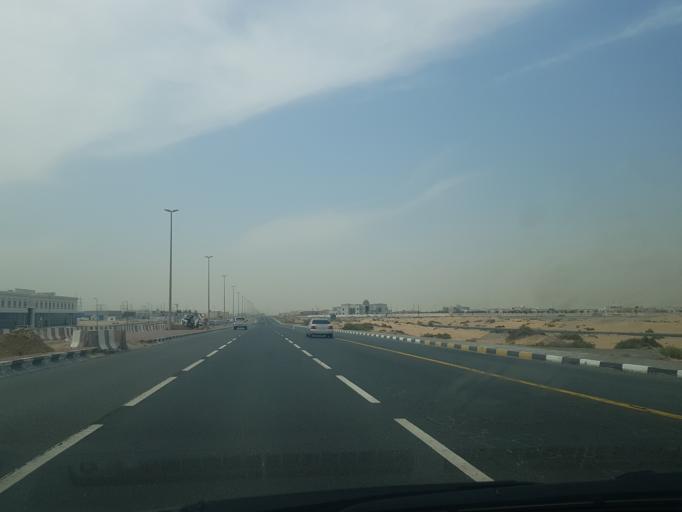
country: AE
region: Ash Shariqah
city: Sharjah
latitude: 25.2580
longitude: 55.5148
